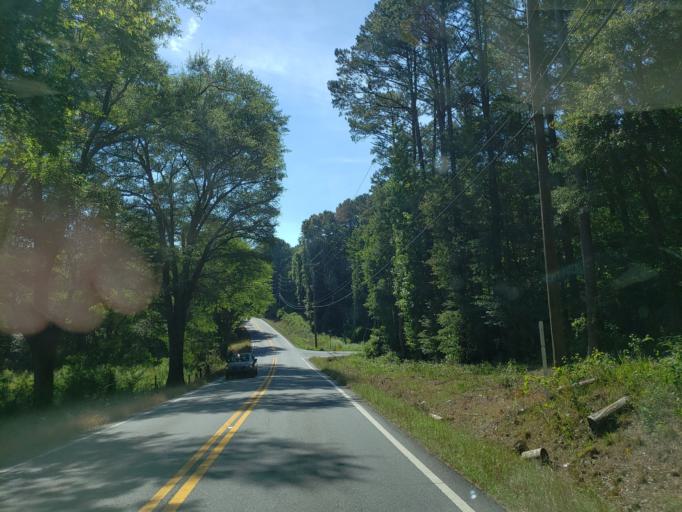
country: US
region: Georgia
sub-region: Cherokee County
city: Woodstock
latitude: 34.1101
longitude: -84.4414
